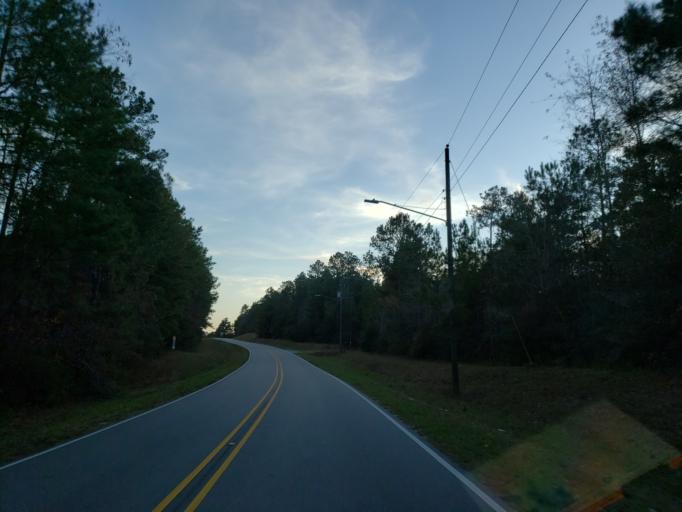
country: US
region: Mississippi
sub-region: Forrest County
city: Hattiesburg
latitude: 31.2608
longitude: -89.3138
